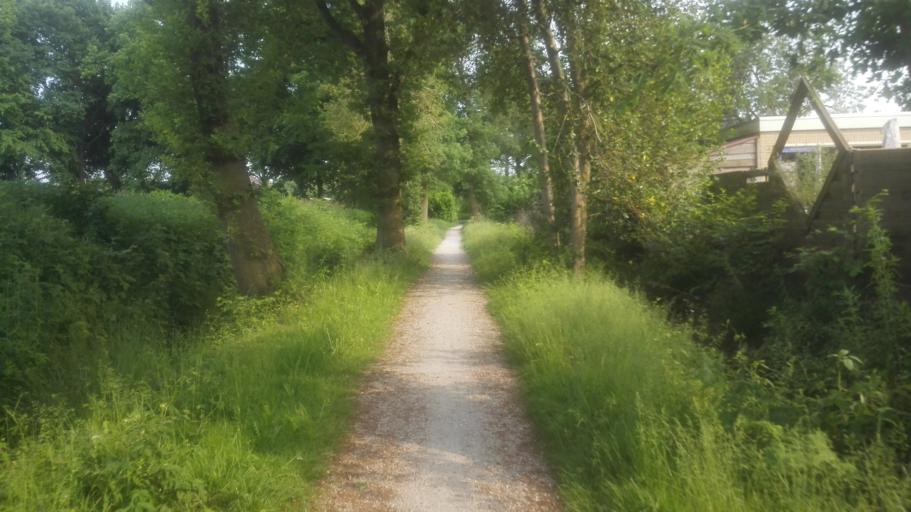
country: NL
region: Friesland
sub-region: Gemeente Weststellingwerf
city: Noordwolde
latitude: 52.9364
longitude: 6.1320
